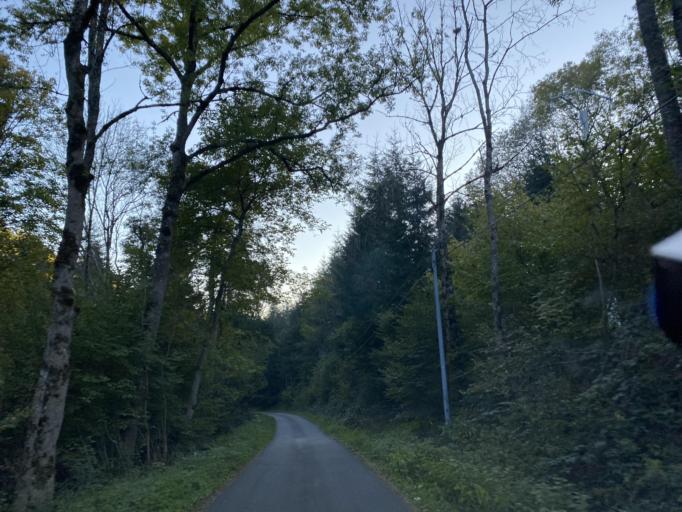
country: FR
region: Rhone-Alpes
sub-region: Departement de la Loire
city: Saint-Just-en-Chevalet
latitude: 45.9304
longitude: 3.8518
